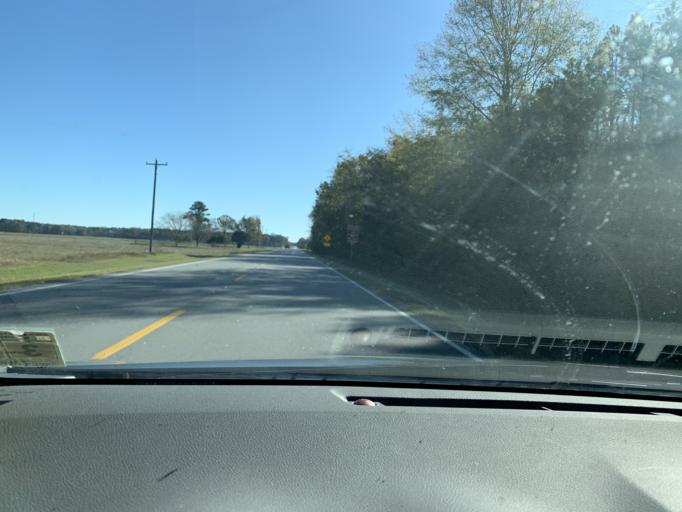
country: US
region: Georgia
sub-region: Coffee County
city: Broxton
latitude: 31.7666
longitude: -83.0125
